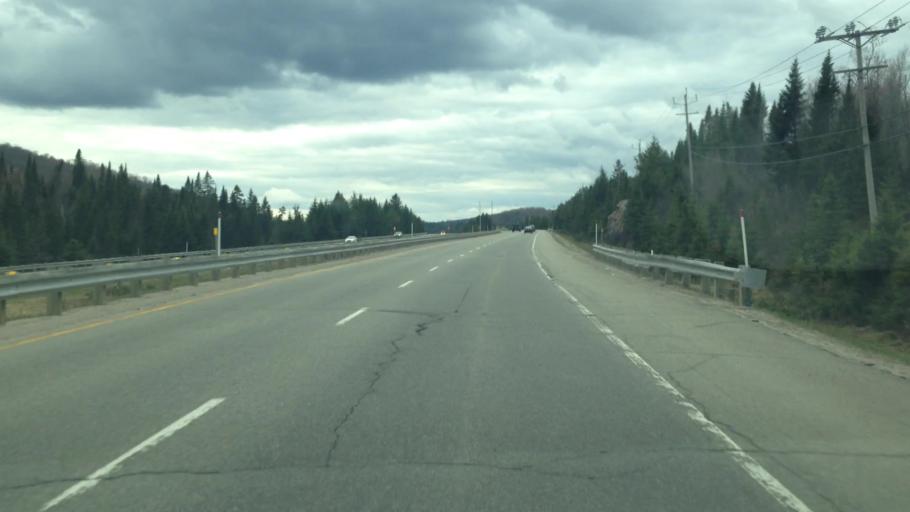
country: CA
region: Quebec
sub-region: Laurentides
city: Sainte-Agathe-des-Monts
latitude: 46.0926
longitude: -74.3392
